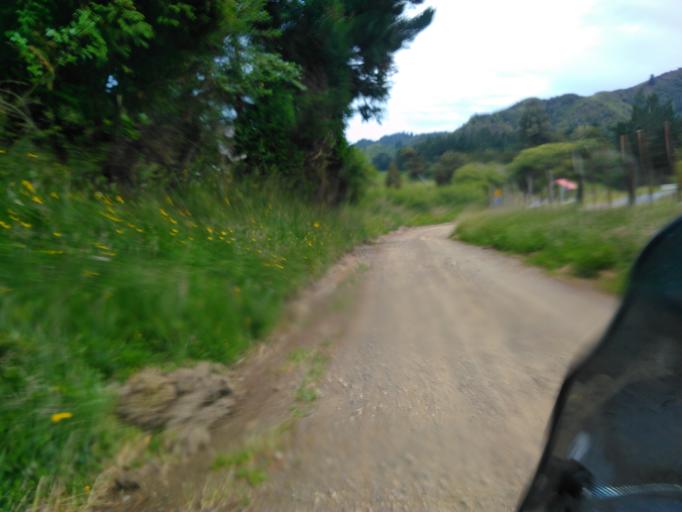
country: NZ
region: Bay of Plenty
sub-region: Opotiki District
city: Opotiki
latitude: -38.1106
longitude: 177.5074
